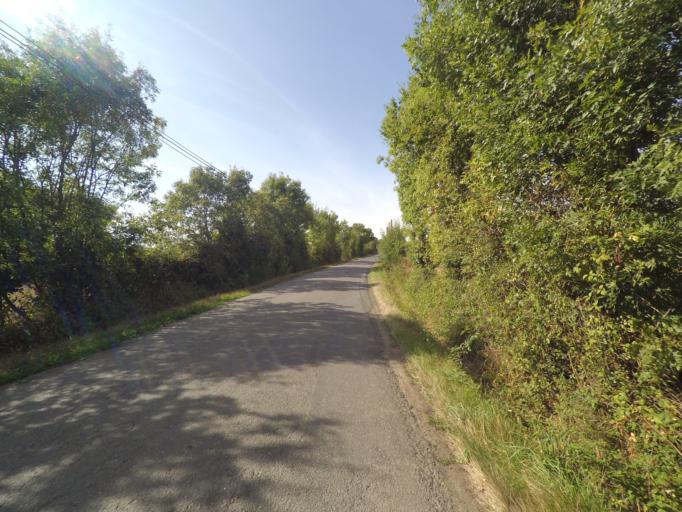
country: FR
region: Pays de la Loire
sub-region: Departement de la Loire-Atlantique
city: Vieillevigne
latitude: 46.9626
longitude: -1.4602
